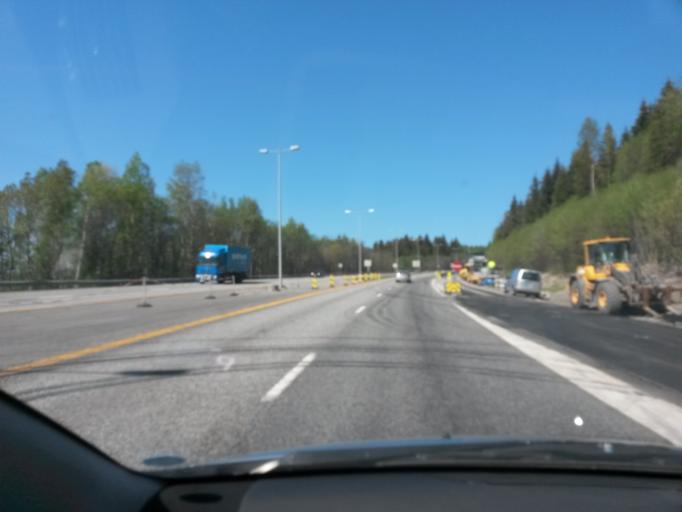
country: NO
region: Buskerud
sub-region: Lier
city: Tranby
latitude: 59.7964
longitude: 10.2681
